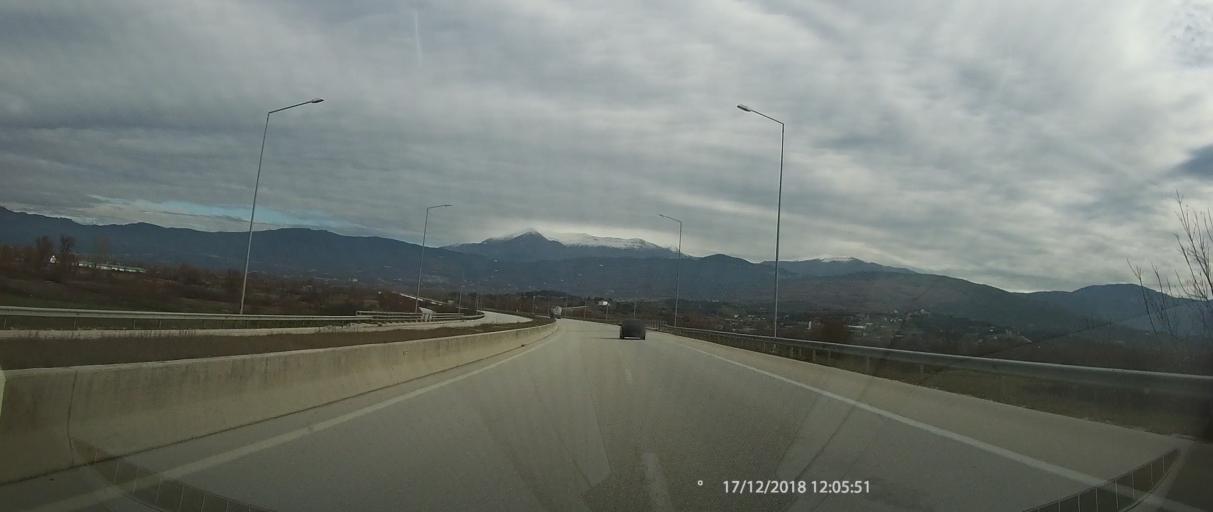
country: GR
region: Epirus
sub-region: Nomos Ioanninon
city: Koutselio
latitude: 39.5982
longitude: 20.9226
